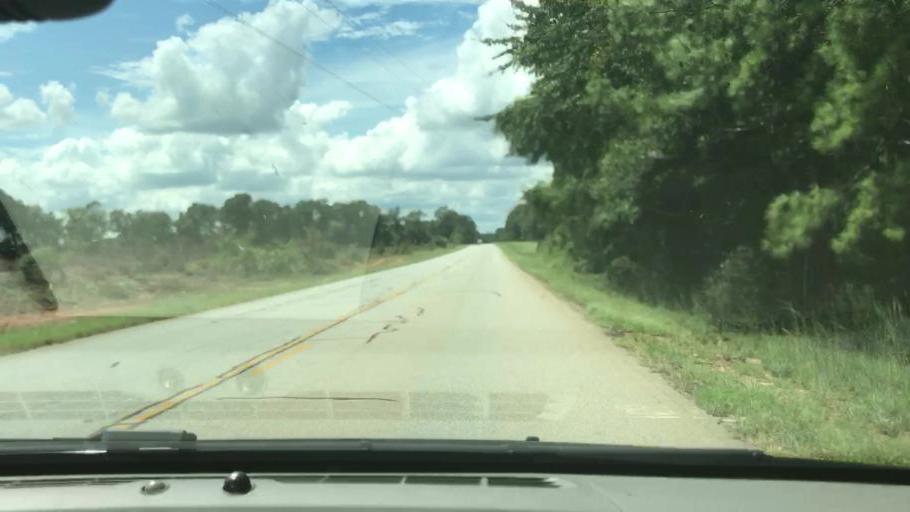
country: US
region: Georgia
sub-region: Stewart County
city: Lumpkin
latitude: 32.1374
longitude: -84.9729
